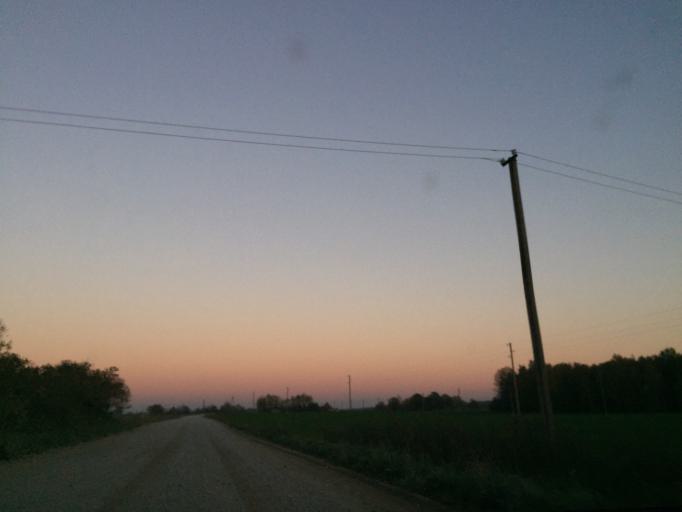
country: LT
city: Akmene
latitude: 56.3775
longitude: 22.7062
